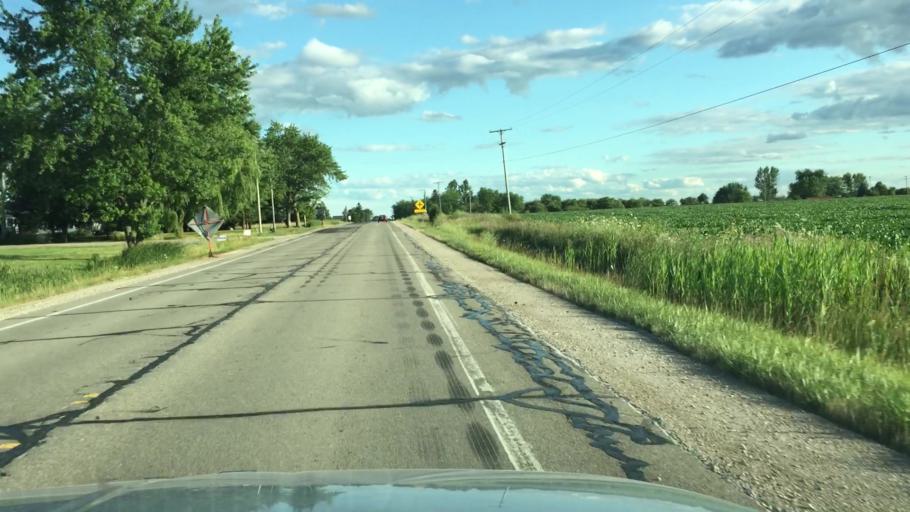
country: US
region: Michigan
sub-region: Saint Clair County
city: Yale
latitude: 43.0905
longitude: -82.7662
